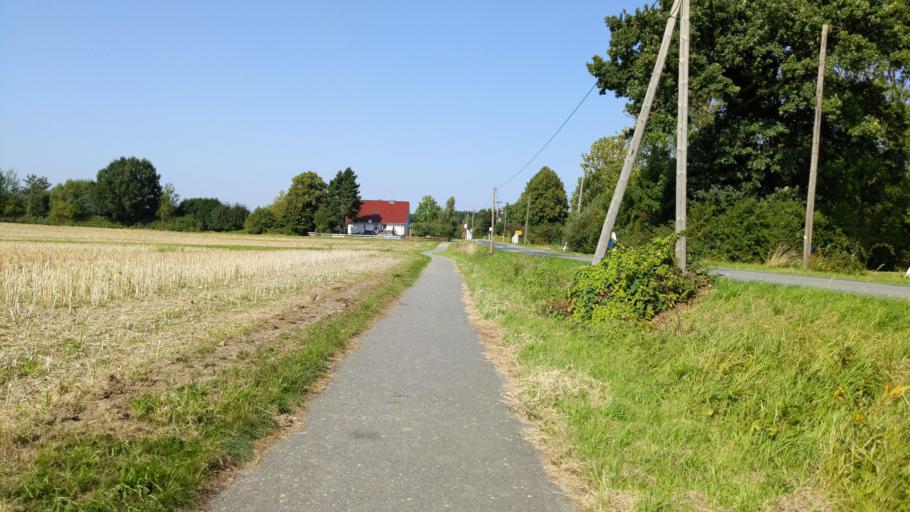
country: DE
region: Schleswig-Holstein
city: Klein Wesenberg
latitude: 53.8051
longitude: 10.5484
